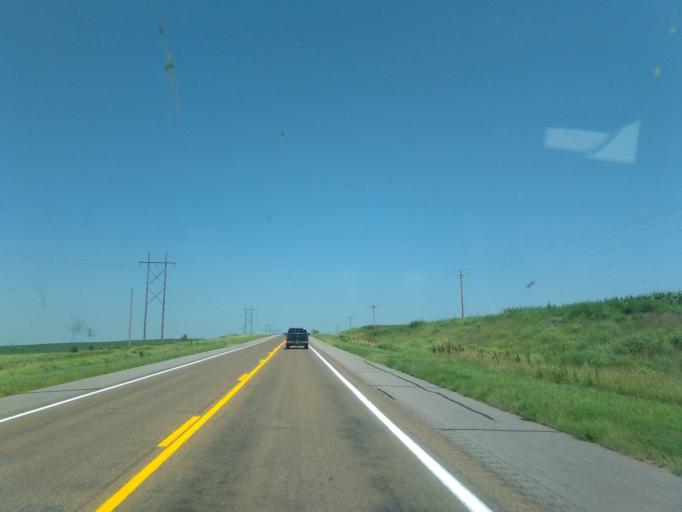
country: US
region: Nebraska
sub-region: Lincoln County
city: North Platte
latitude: 40.8094
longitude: -100.7536
